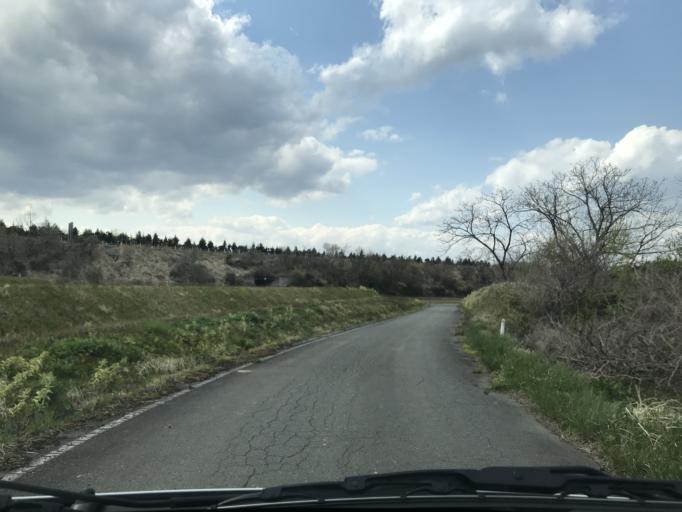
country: JP
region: Iwate
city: Mizusawa
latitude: 39.0721
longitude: 141.1017
